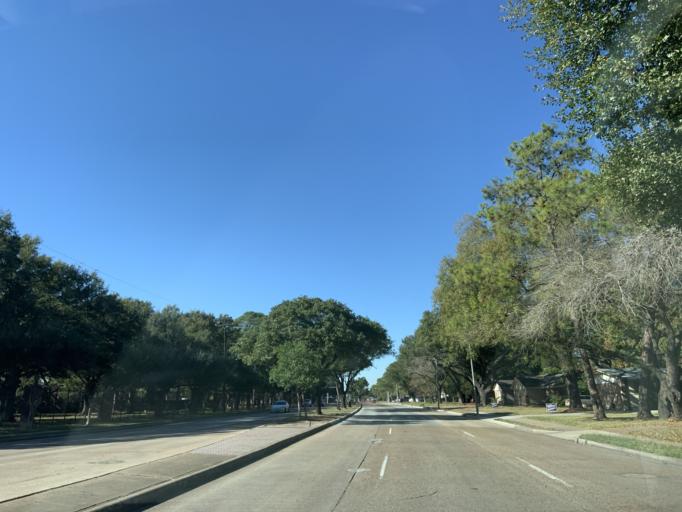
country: US
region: Texas
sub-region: Harris County
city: Bellaire
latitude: 29.6955
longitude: -95.5121
